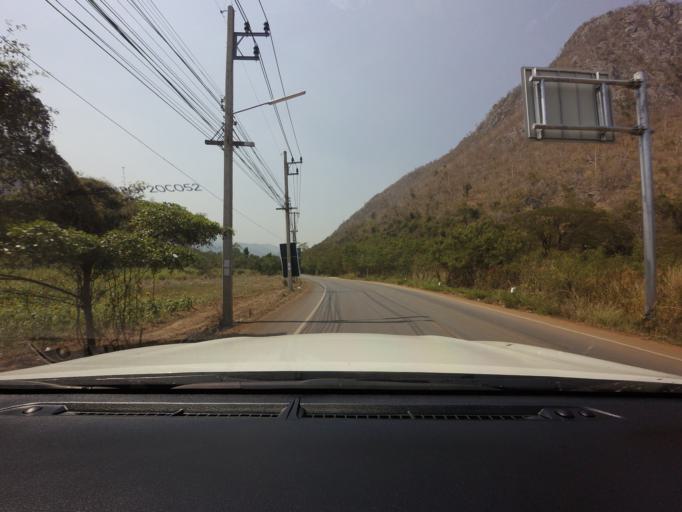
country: TH
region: Nakhon Ratchasima
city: Pak Chong
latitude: 14.5414
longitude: 101.3515
